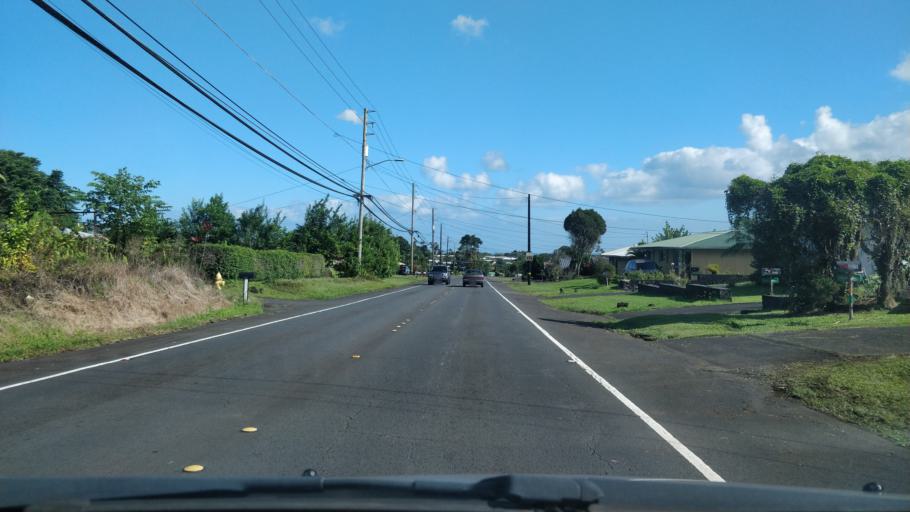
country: US
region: Hawaii
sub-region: Hawaii County
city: Hilo
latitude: 19.6739
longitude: -155.0919
